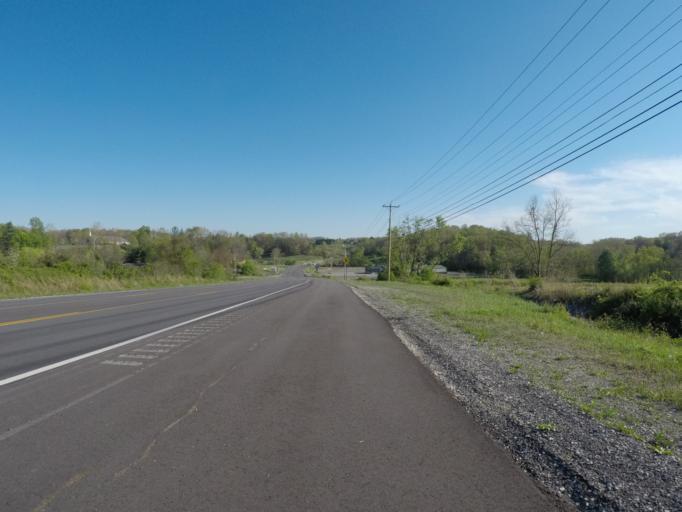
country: US
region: Kentucky
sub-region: Boyd County
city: Meads
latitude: 38.3607
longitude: -82.6980
